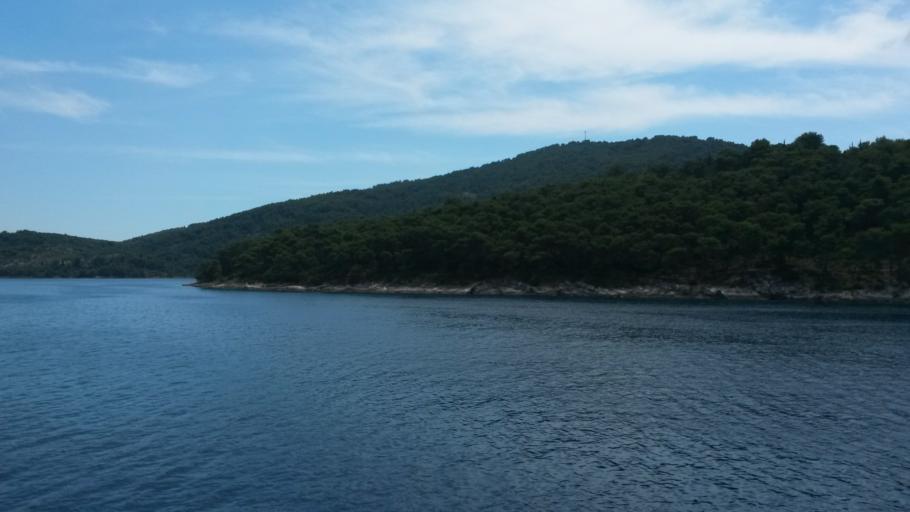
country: HR
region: Dubrovacko-Neretvanska
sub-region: Grad Dubrovnik
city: Vela Luka
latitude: 42.9641
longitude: 16.6805
